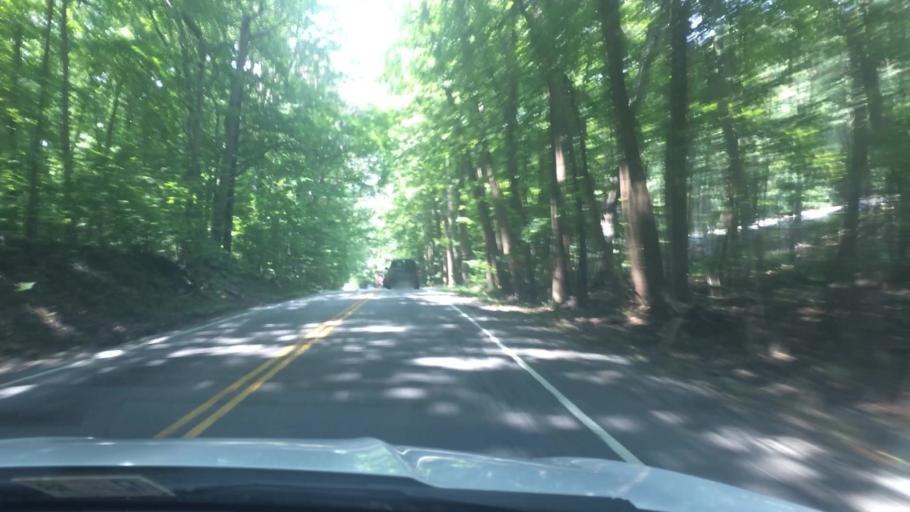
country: US
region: Virginia
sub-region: York County
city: Yorktown
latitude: 37.2066
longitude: -76.5843
